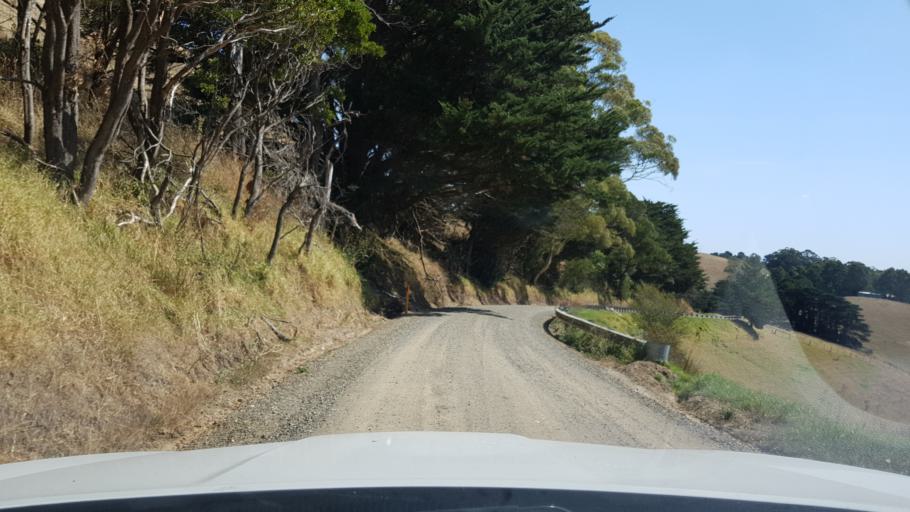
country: AU
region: Victoria
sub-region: Baw Baw
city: Warragul
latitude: -38.2986
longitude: 145.9119
